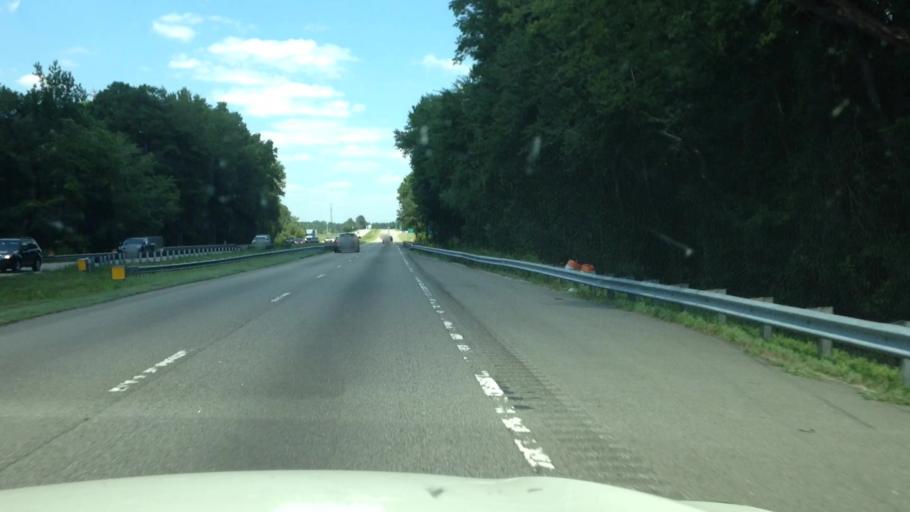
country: US
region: North Carolina
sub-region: Robeson County
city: Saint Pauls
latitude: 34.8022
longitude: -78.9899
